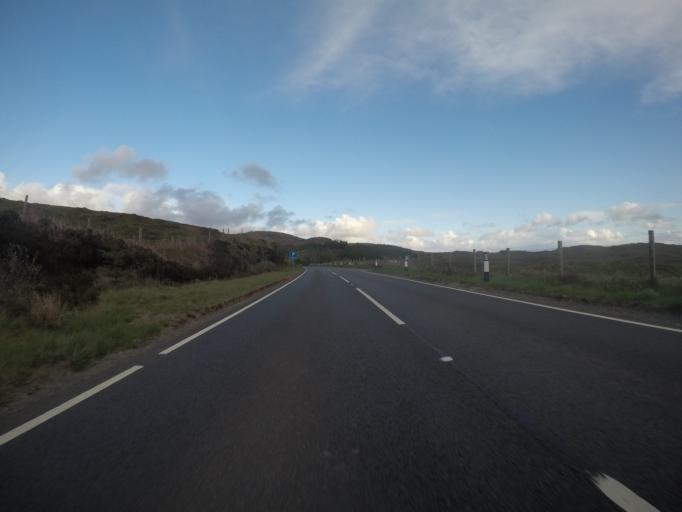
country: GB
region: Scotland
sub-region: Highland
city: Portree
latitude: 57.5326
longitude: -6.3551
